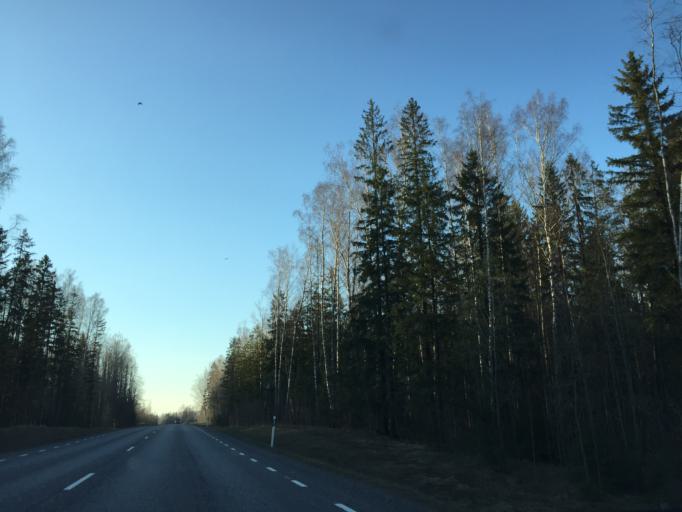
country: EE
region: Ida-Virumaa
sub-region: Johvi vald
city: Johvi
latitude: 59.3310
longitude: 27.4802
